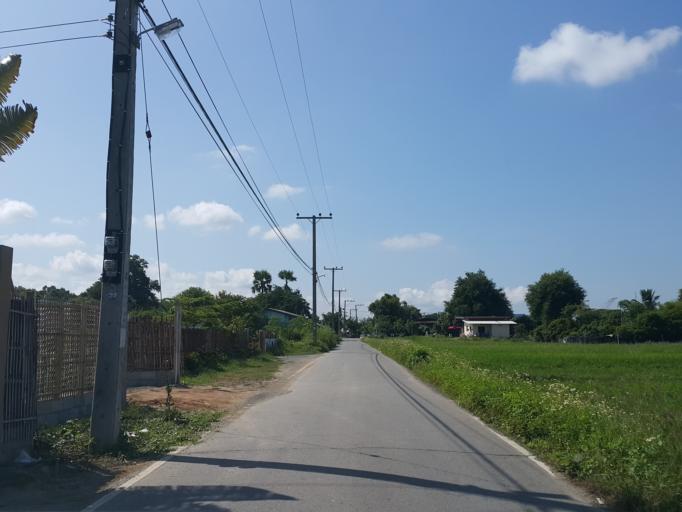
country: TH
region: Chiang Mai
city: San Kamphaeng
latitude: 18.7546
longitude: 99.1701
